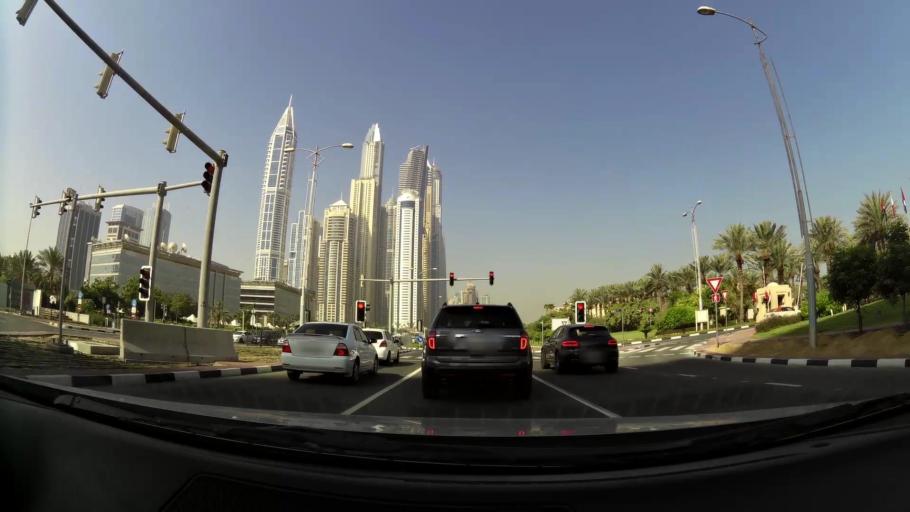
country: AE
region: Dubai
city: Dubai
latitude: 25.0956
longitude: 55.1525
